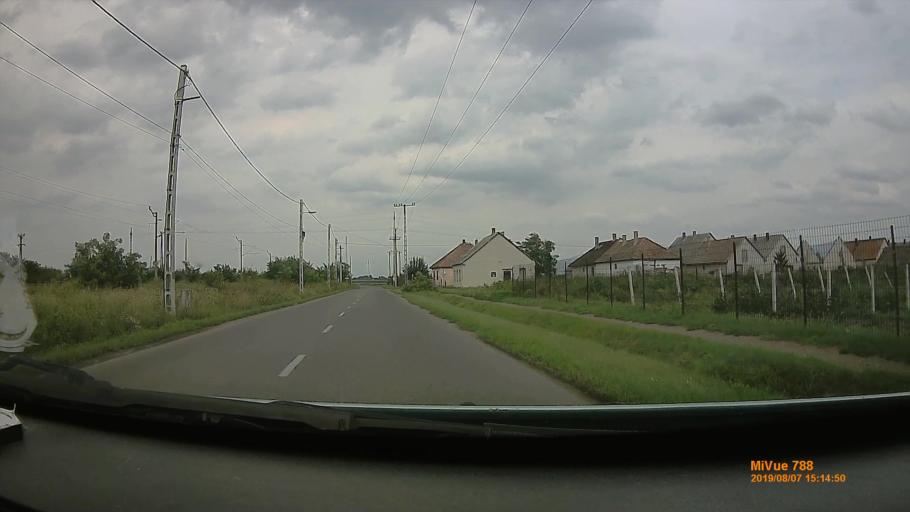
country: HU
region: Borsod-Abauj-Zemplen
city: Encs
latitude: 48.3343
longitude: 21.1257
